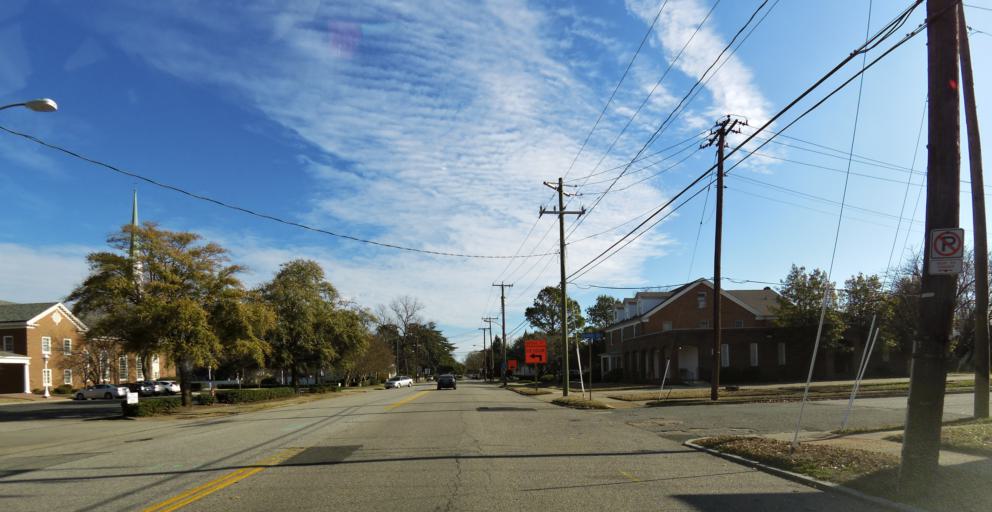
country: US
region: Virginia
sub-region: City of Hampton
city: Hampton
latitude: 37.0200
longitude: -76.3513
